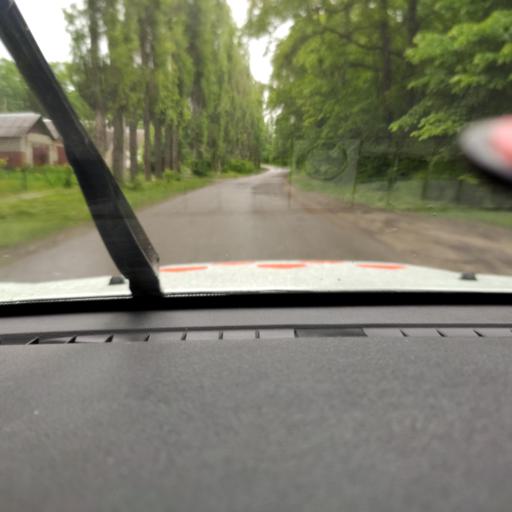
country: RU
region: Voronezj
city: Devitsa
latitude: 51.6058
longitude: 38.9943
